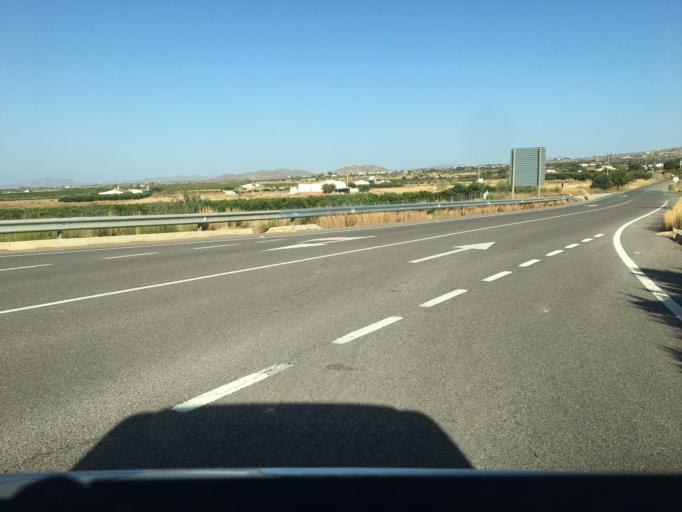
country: ES
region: Andalusia
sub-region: Provincia de Almeria
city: Huercal-Overa
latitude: 37.4659
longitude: -1.8841
